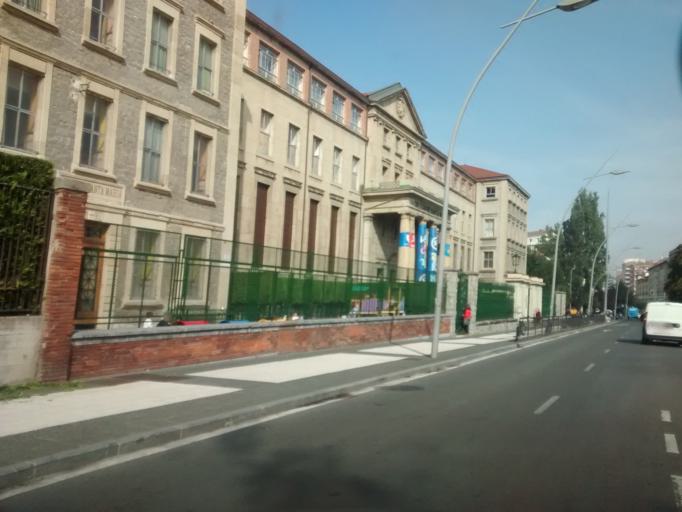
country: ES
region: Basque Country
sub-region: Provincia de Alava
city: Gasteiz / Vitoria
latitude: 42.8447
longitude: -2.6786
